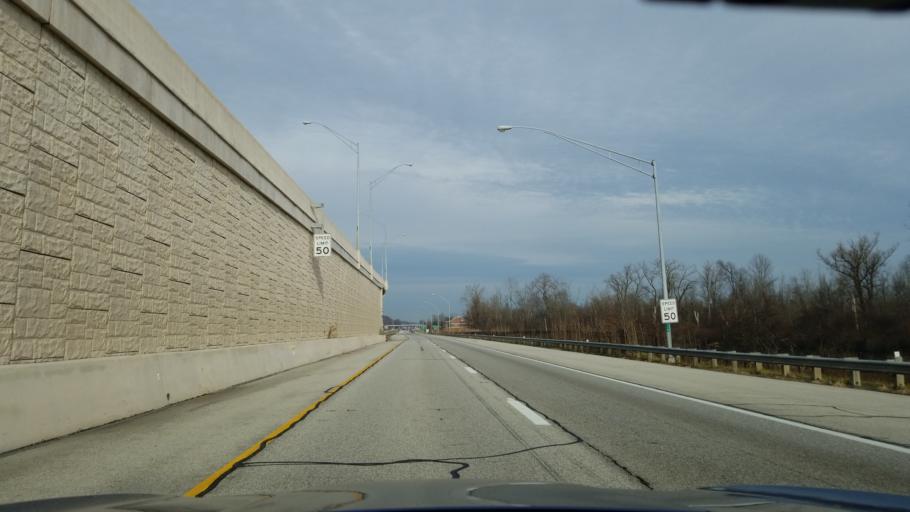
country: US
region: Ohio
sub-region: Summit County
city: Macedonia
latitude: 41.2919
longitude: -81.5107
